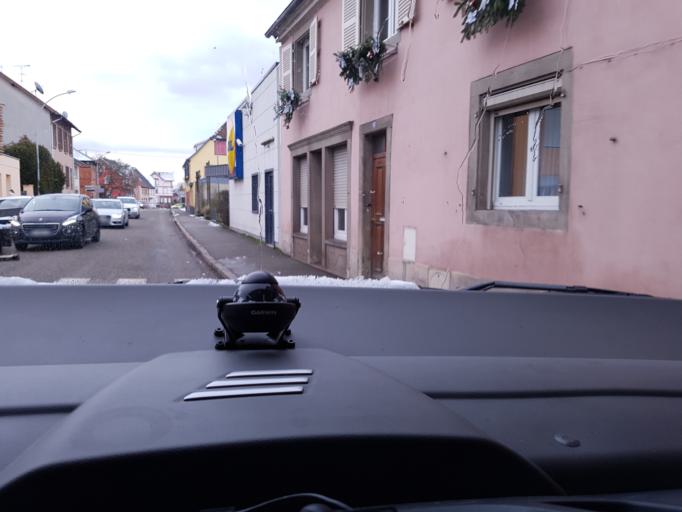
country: FR
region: Alsace
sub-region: Departement du Bas-Rhin
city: Ville
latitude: 48.3438
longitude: 7.3067
